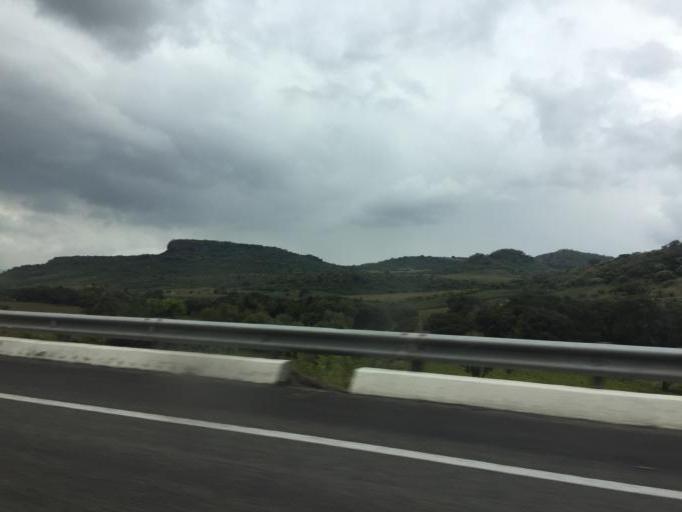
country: MX
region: Jalisco
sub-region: Zapotlan del Rey
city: Zapotlan del Rey
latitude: 20.4896
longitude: -102.9429
